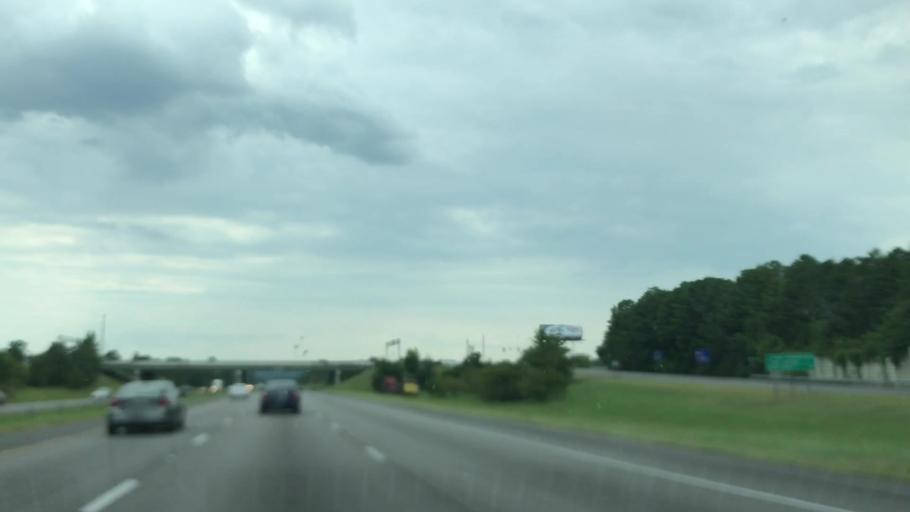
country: US
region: South Carolina
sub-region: Richland County
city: Woodfield
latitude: 34.0235
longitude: -80.9456
